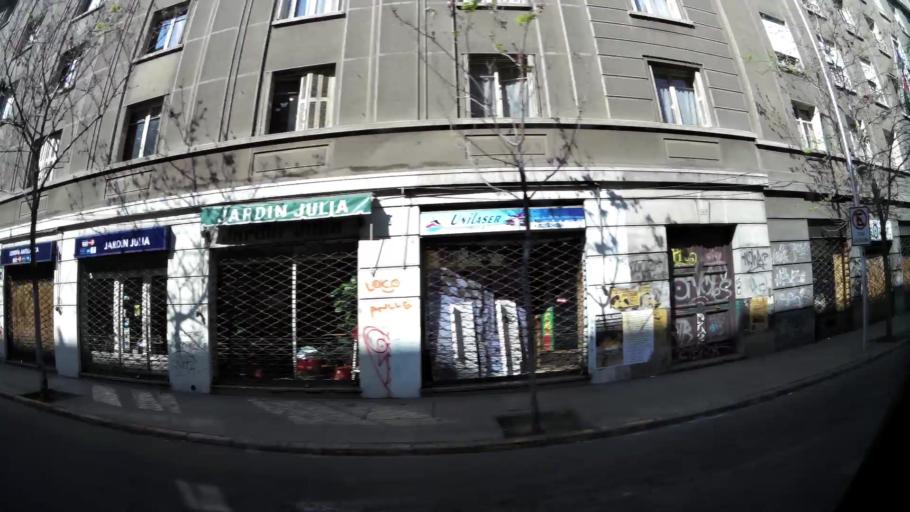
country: CL
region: Santiago Metropolitan
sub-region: Provincia de Santiago
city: Santiago
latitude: -33.4408
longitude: -70.6578
